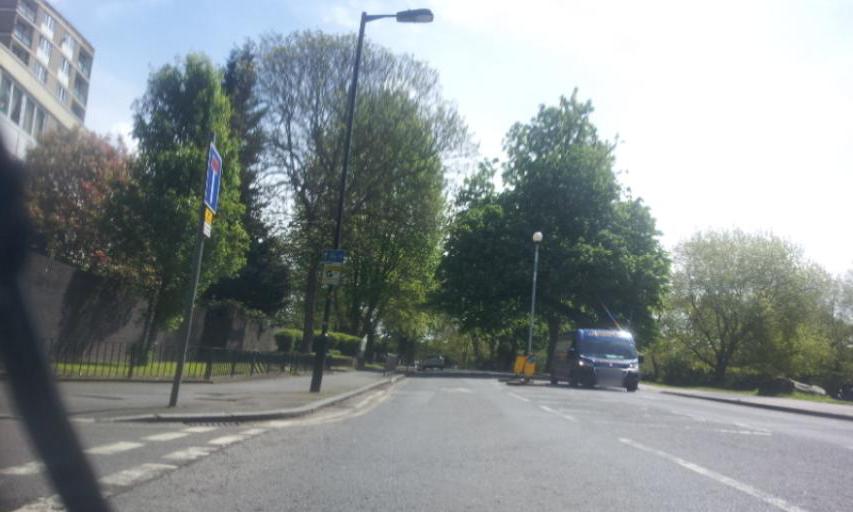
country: GB
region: England
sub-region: Greater London
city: Camberwell
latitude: 51.4593
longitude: -0.0576
